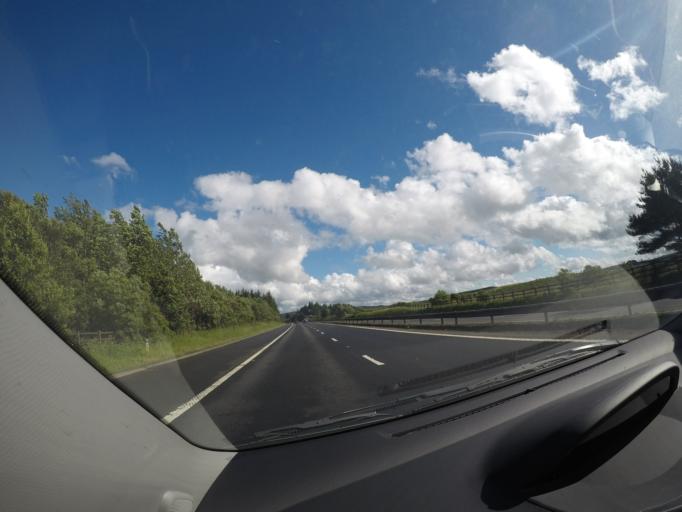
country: GB
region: Scotland
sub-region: South Lanarkshire
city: Douglas
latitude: 55.5913
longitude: -3.8309
